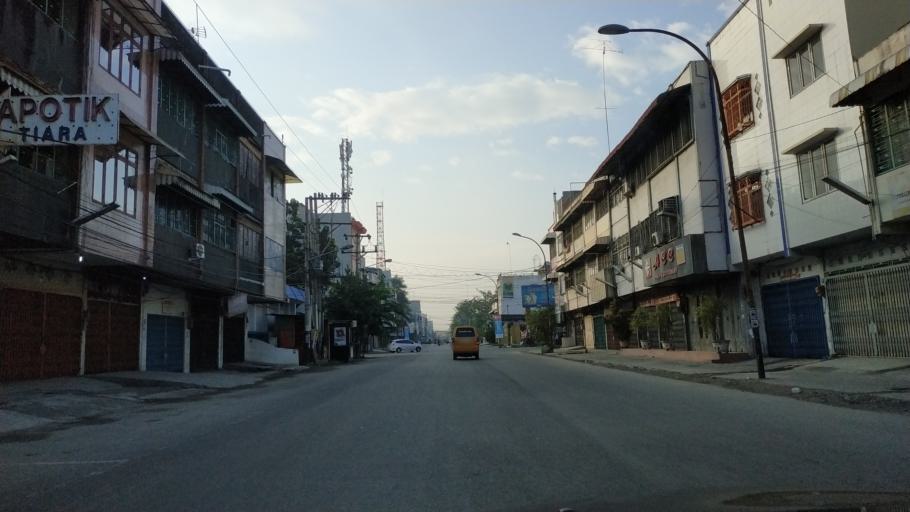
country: ID
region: North Sumatra
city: Medan
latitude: 3.5937
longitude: 98.6886
